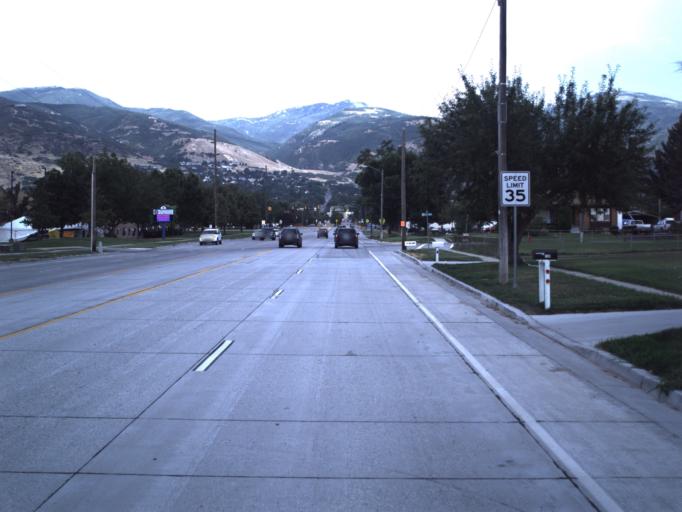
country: US
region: Utah
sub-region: Davis County
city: Bountiful
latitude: 40.8936
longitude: -111.8839
